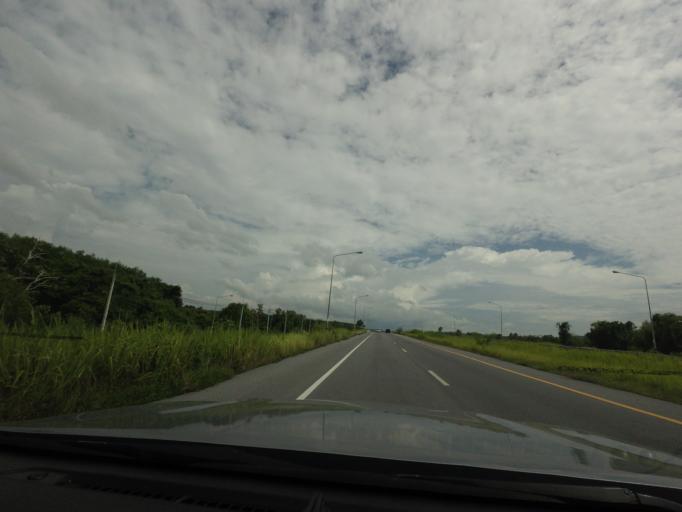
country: TH
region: Pattani
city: Mae Lan
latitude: 6.6565
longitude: 101.2353
